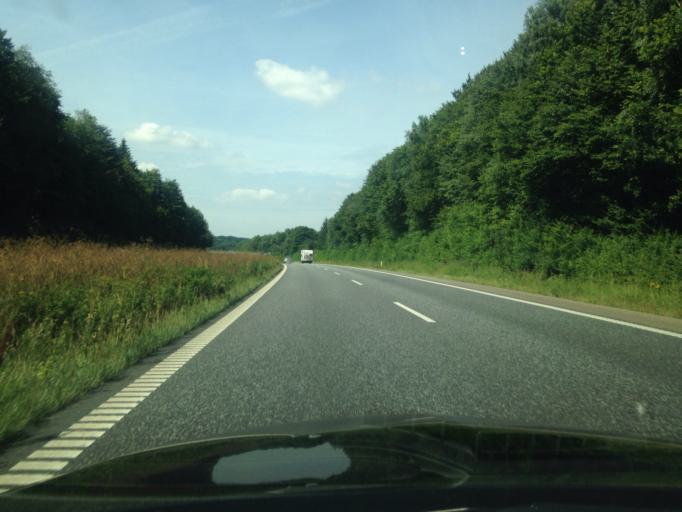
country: DK
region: South Denmark
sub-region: Fredericia Kommune
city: Taulov
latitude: 55.5424
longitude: 9.6098
